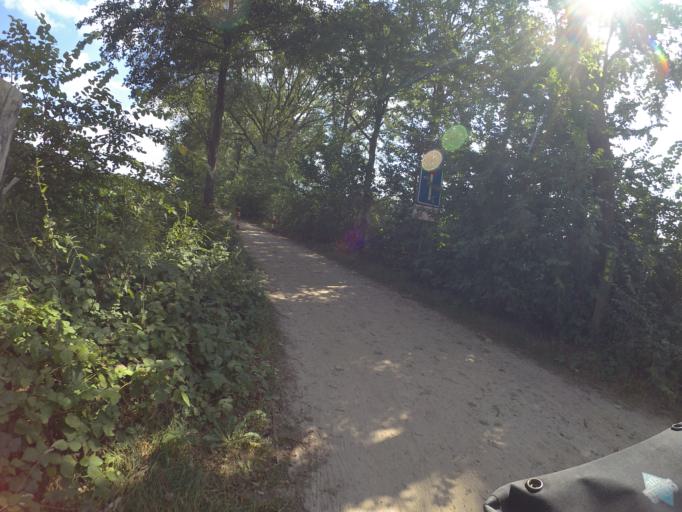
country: NL
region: North Brabant
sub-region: Gemeente Sint-Oedenrode
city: Sint-Oedenrode
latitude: 51.5870
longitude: 5.4387
